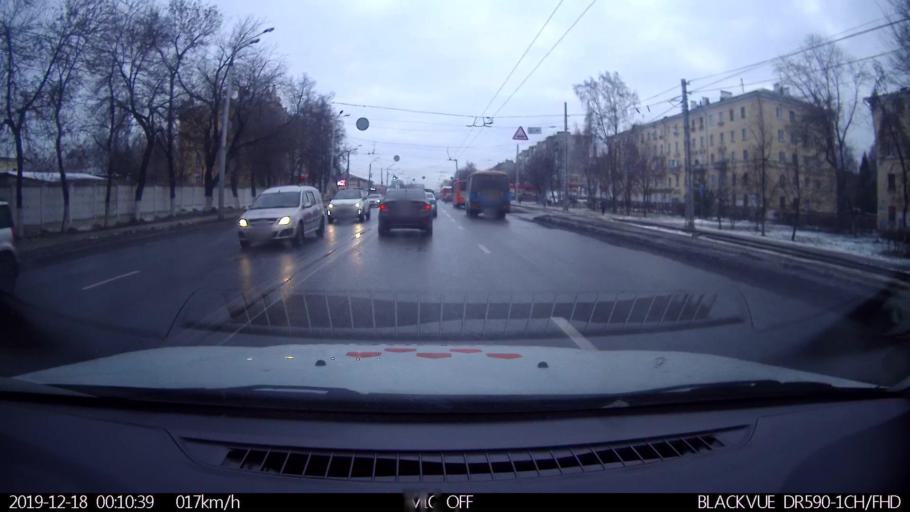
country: RU
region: Nizjnij Novgorod
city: Neklyudovo
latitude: 56.3421
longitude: 43.8772
